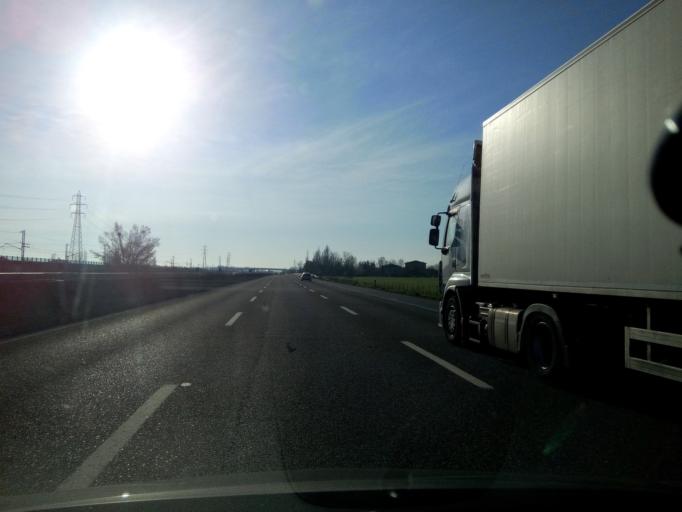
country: IT
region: Emilia-Romagna
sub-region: Provincia di Parma
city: San Prospero
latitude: 44.8147
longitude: 10.4112
